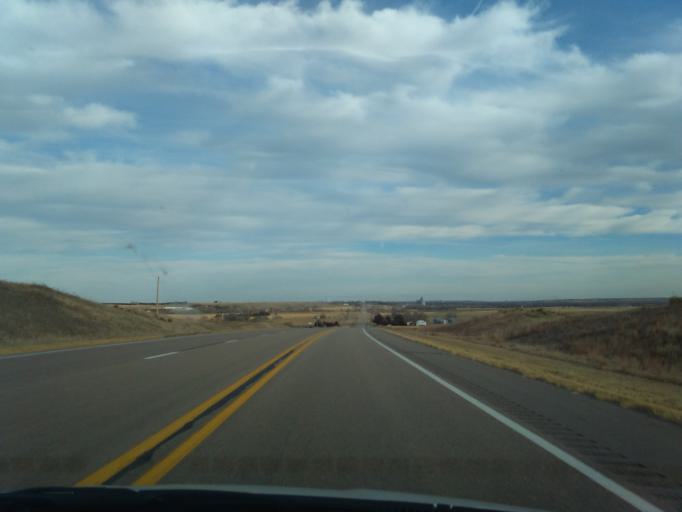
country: US
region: Nebraska
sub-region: Hitchcock County
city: Trenton
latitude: 40.2343
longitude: -100.9045
